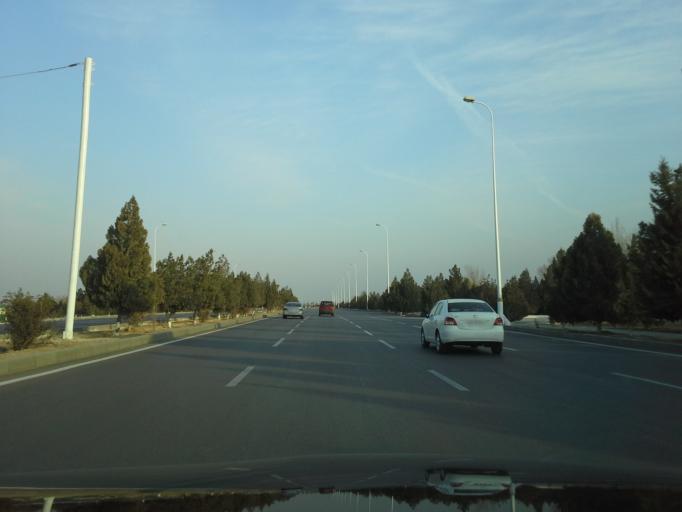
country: TM
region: Ahal
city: Abadan
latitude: 38.0504
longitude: 58.1880
